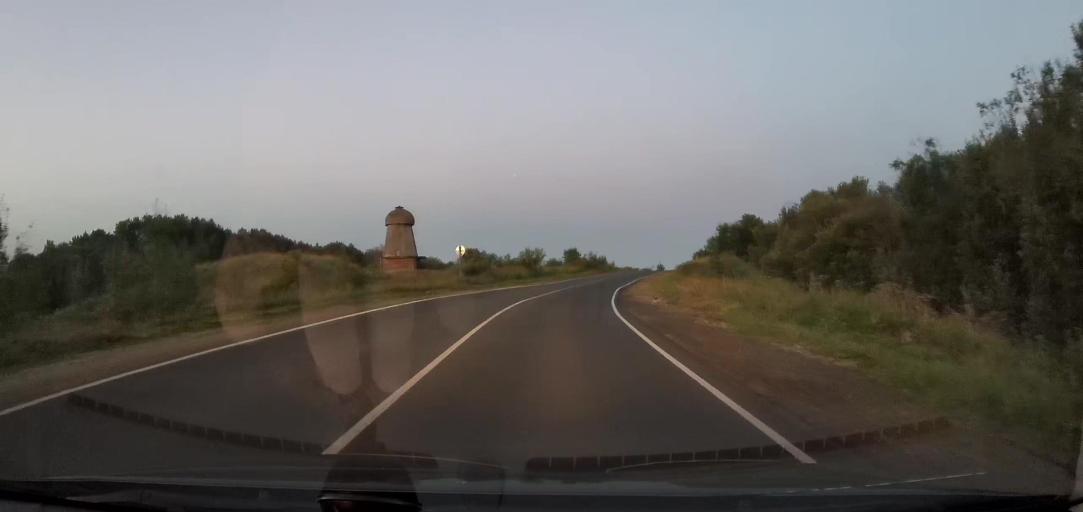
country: RU
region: Arkhangelskaya
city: Uyemskiy
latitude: 64.4498
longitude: 40.9438
